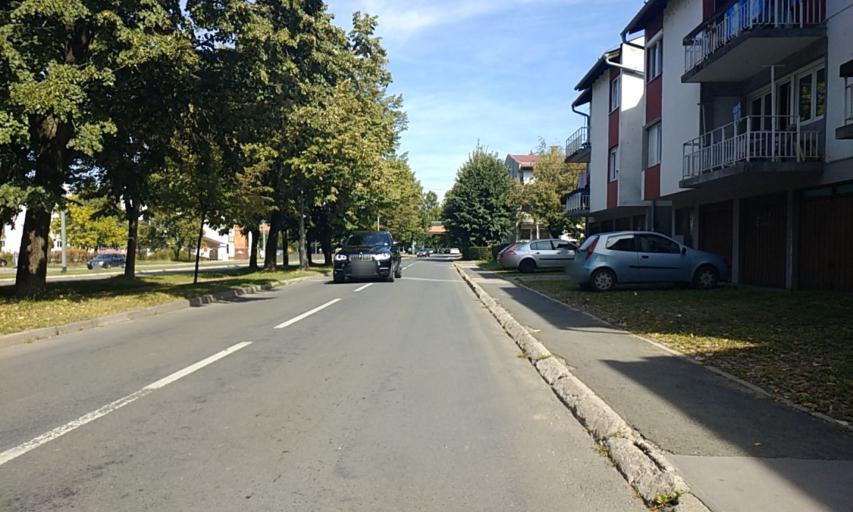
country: BA
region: Republika Srpska
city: Starcevica
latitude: 44.7633
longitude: 17.2058
